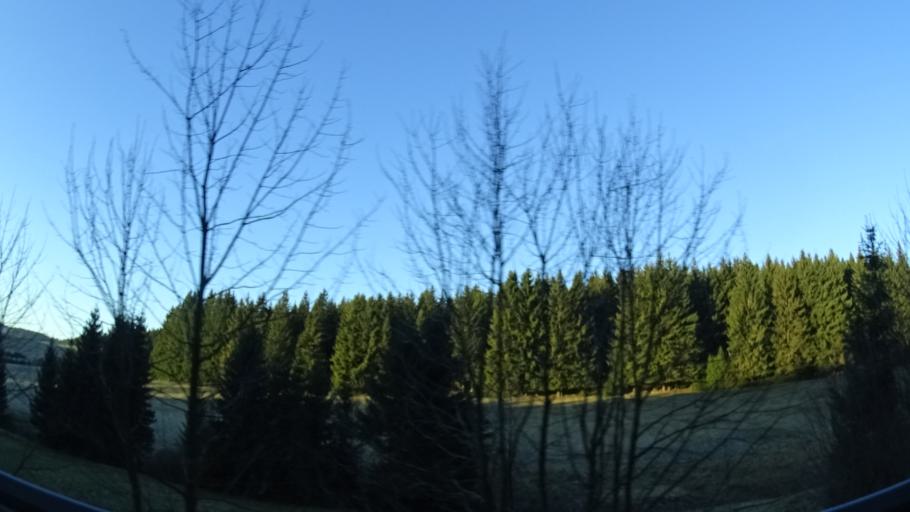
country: DE
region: Bavaria
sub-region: Upper Franconia
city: Tettau
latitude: 50.4837
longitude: 11.2642
